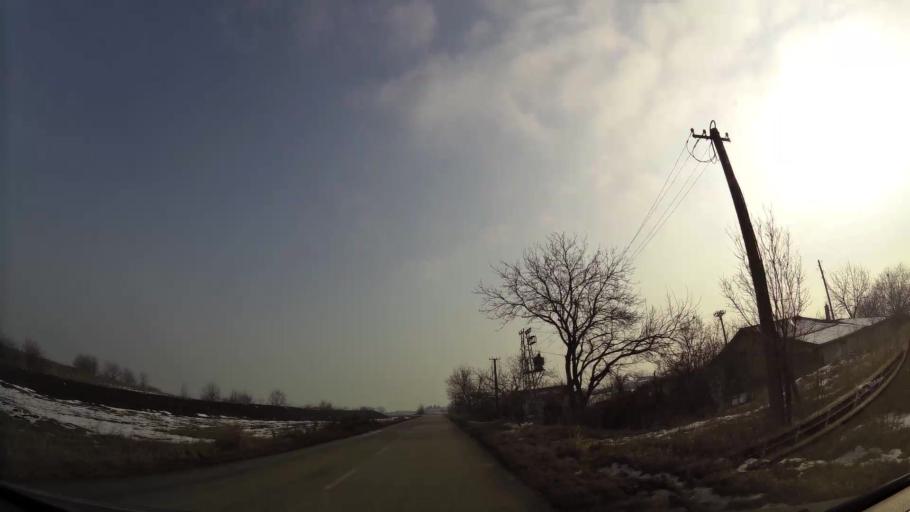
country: MK
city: Kadino
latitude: 41.9742
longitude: 21.6040
